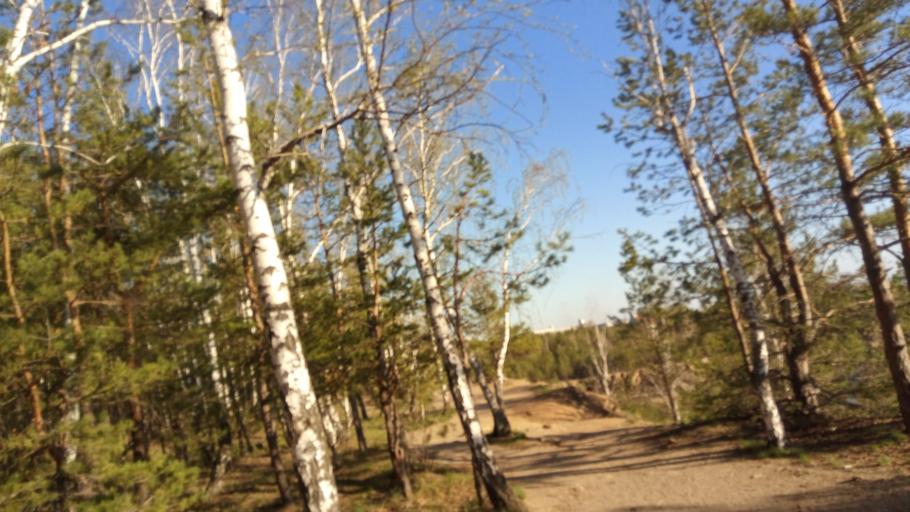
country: RU
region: Chelyabinsk
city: Novosineglazovskiy
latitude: 55.1245
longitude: 61.3368
